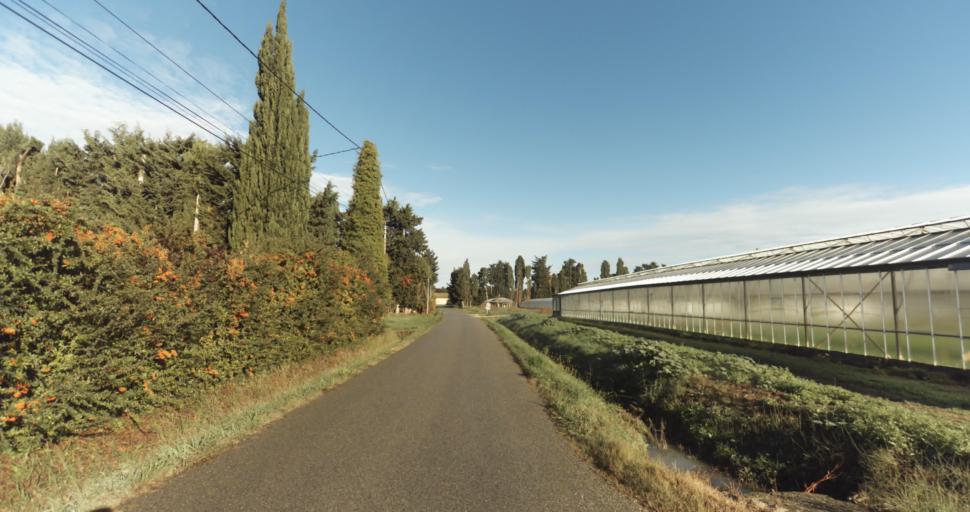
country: FR
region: Provence-Alpes-Cote d'Azur
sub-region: Departement des Bouches-du-Rhone
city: Rognonas
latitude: 43.8898
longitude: 4.7993
